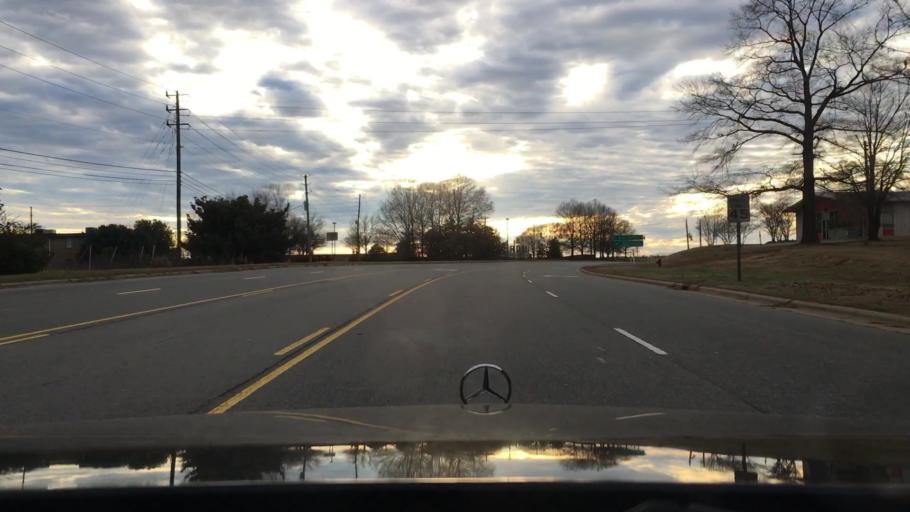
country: US
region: North Carolina
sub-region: Wake County
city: Morrisville
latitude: 35.8989
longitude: -78.7698
